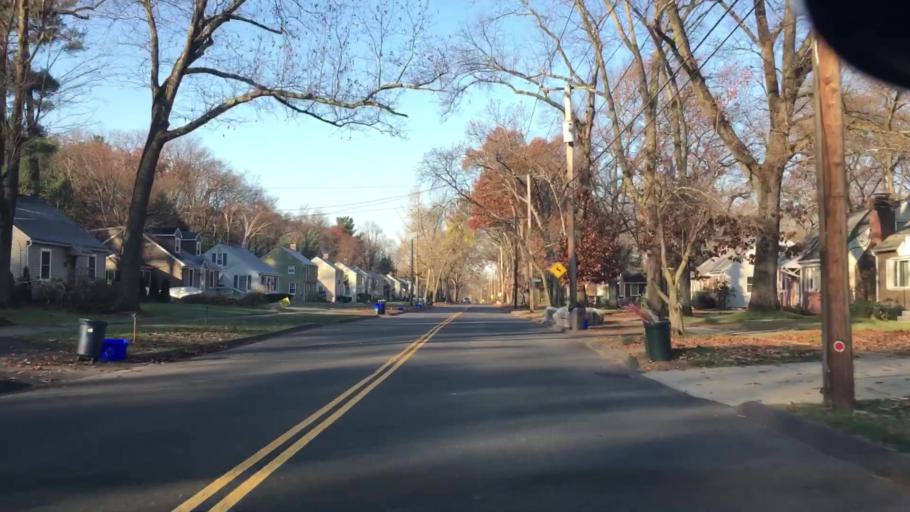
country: US
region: Connecticut
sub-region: Hartford County
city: Sherwood Manor
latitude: 42.0318
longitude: -72.5678
